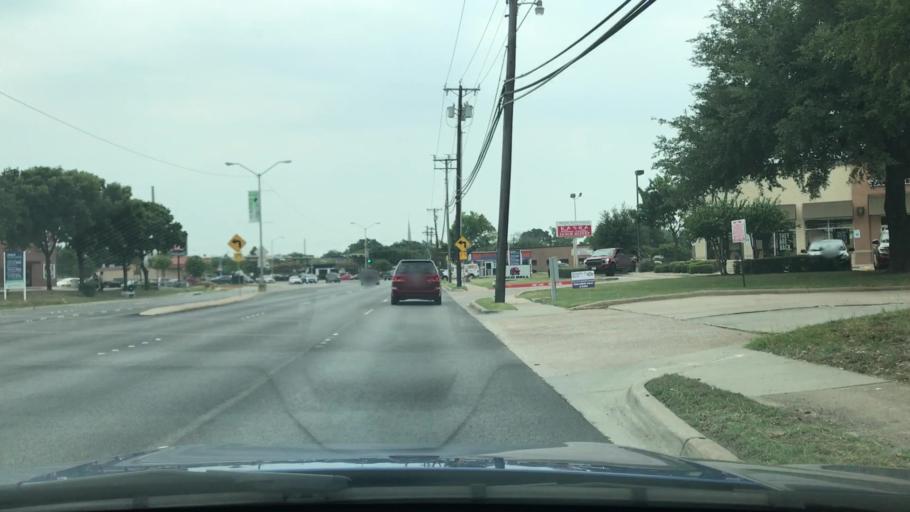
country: US
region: Texas
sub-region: Dallas County
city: Richardson
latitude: 32.9623
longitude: -96.7362
